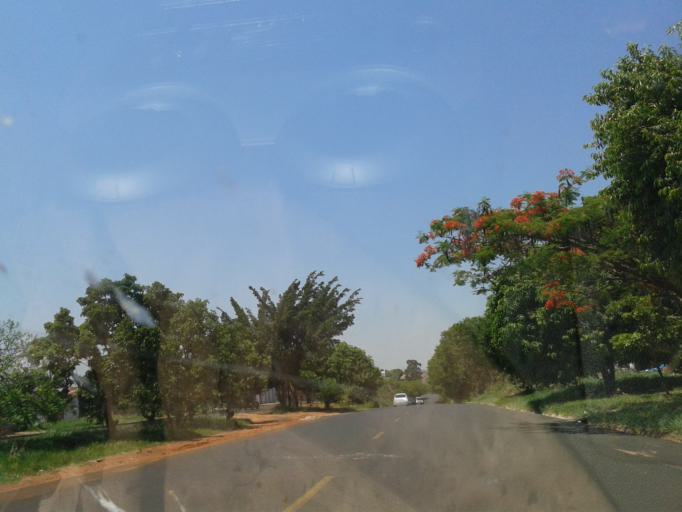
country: BR
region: Minas Gerais
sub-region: Uberlandia
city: Uberlandia
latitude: -18.9497
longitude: -48.3070
